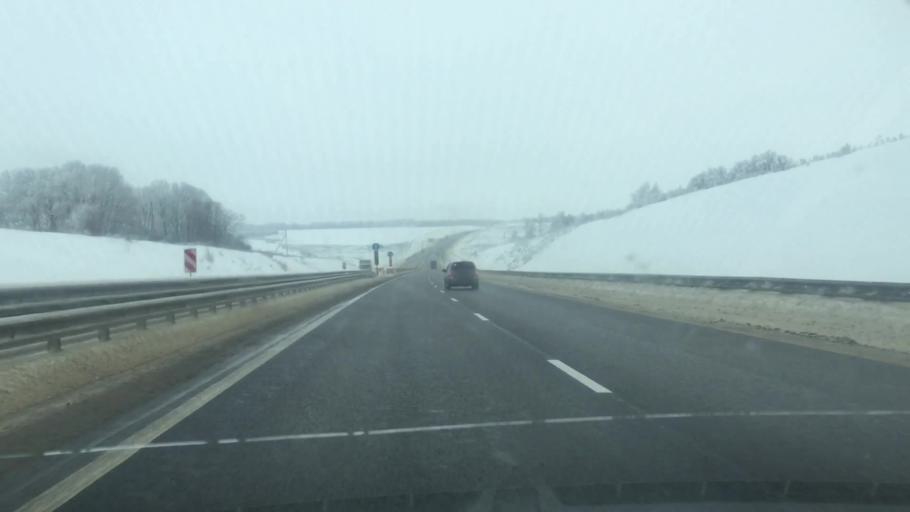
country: RU
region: Lipetsk
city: Stanovoye
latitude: 52.8712
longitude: 38.2803
